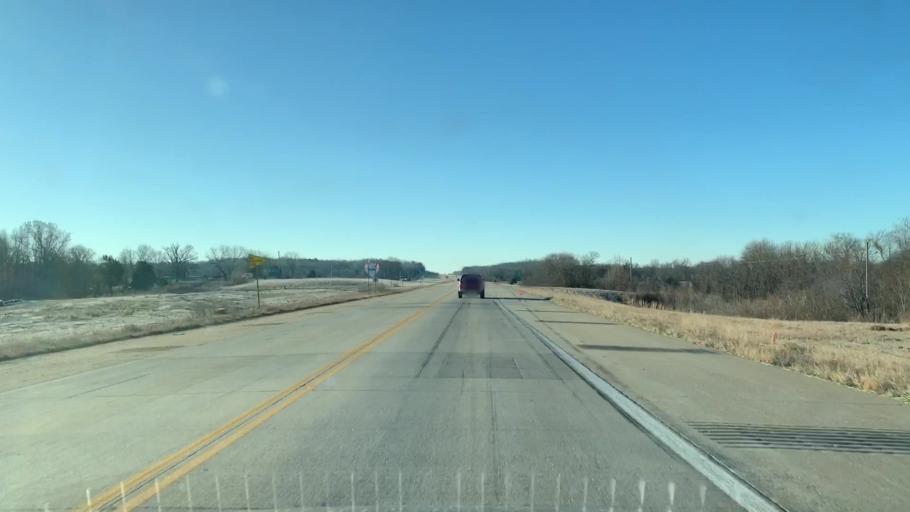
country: US
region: Kansas
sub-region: Crawford County
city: Arma
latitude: 37.6748
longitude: -94.7035
